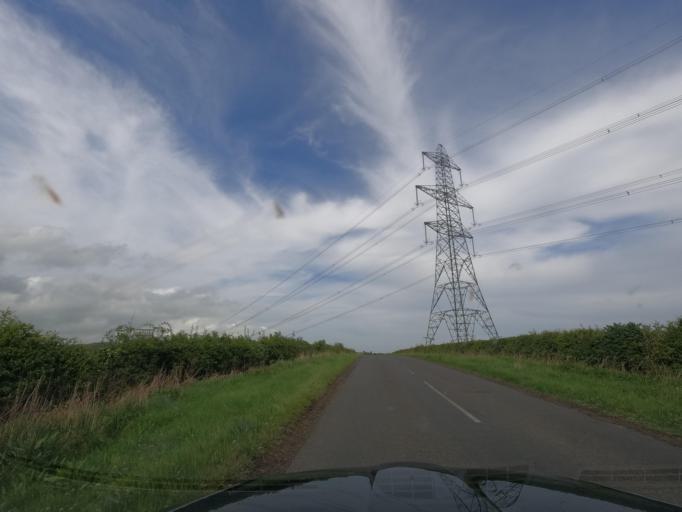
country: GB
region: England
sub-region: Northumberland
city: Whittingham
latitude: 55.4090
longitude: -1.8904
